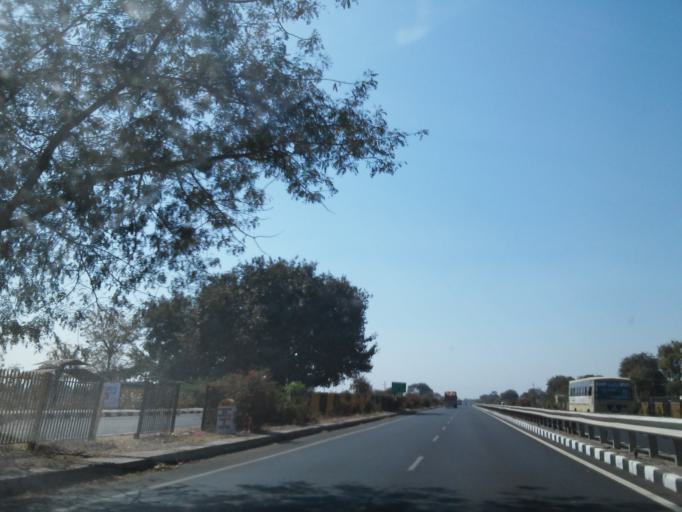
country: IN
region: Gujarat
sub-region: Sabar Kantha
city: Himatnagar
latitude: 23.4861
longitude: 72.8974
